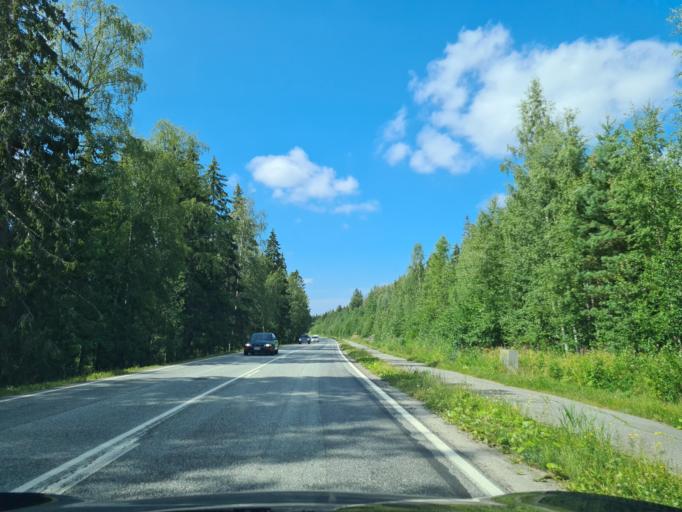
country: FI
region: Ostrobothnia
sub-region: Vaasa
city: Vaasa
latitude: 63.1962
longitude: 21.5453
